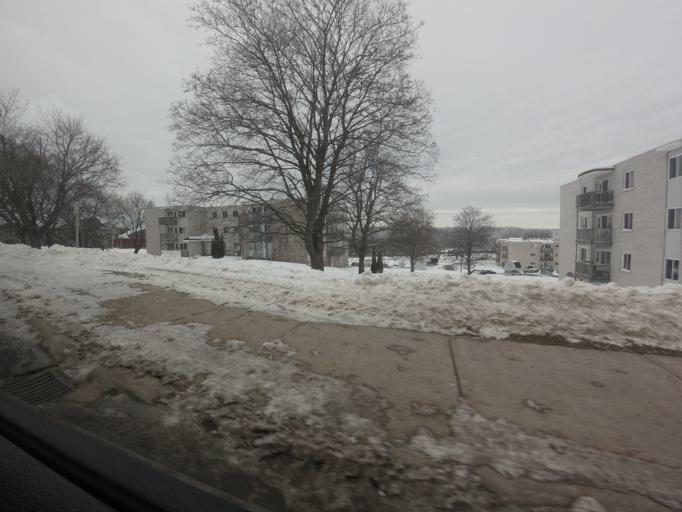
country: CA
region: New Brunswick
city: Oromocto
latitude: 45.8495
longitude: -66.4790
